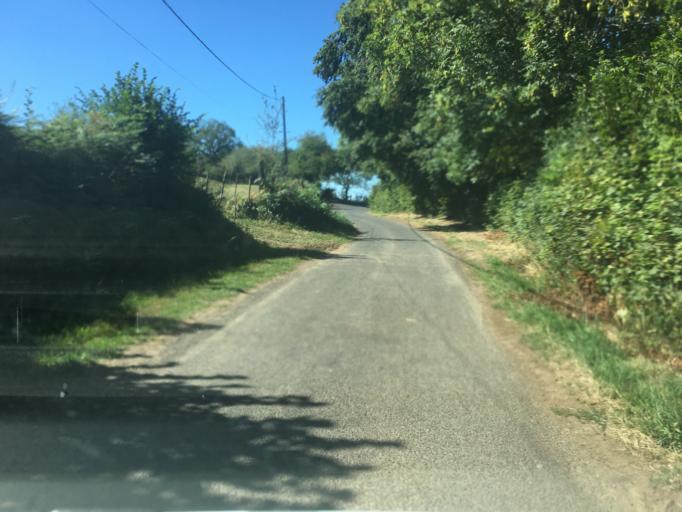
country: FR
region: Limousin
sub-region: Departement de la Correze
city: Bort-les-Orgues
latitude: 45.3989
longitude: 2.4782
